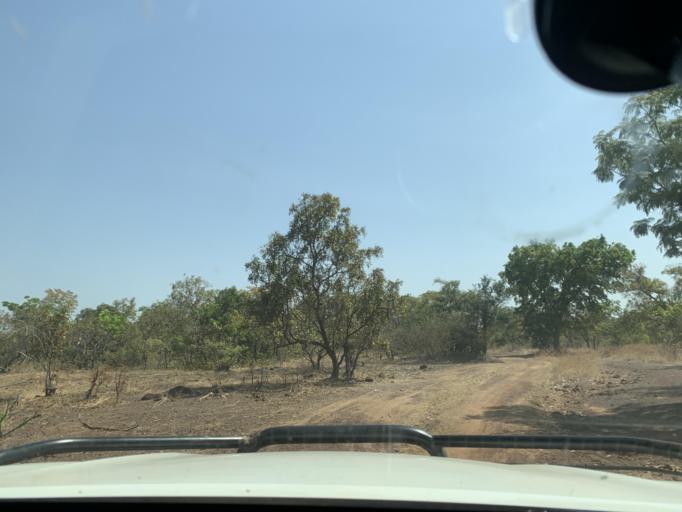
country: ML
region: Sikasso
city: Kolondieba
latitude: 10.8360
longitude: -6.7934
